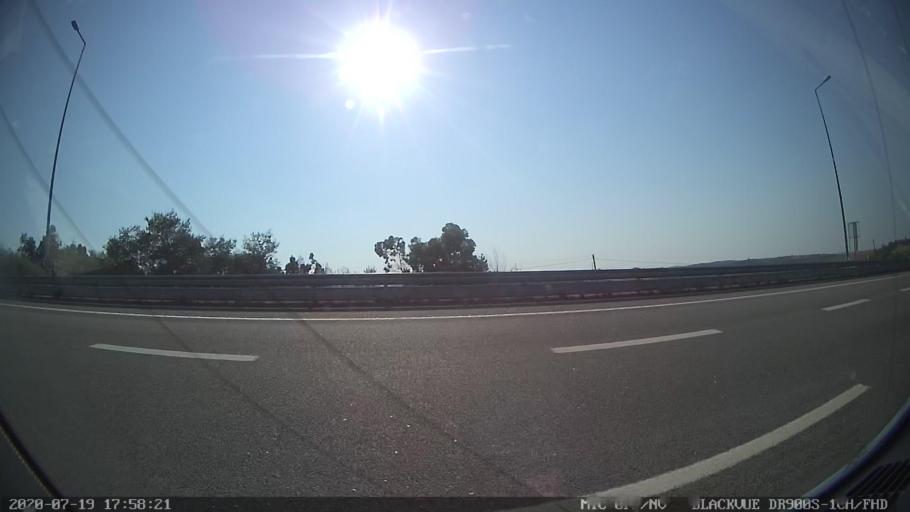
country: PT
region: Braganca
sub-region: Mirandela
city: Mirandela
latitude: 41.5087
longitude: -7.1837
